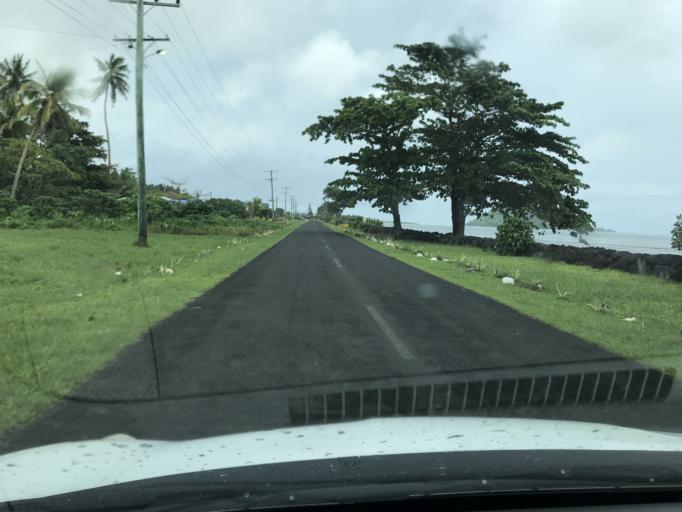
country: WS
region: Va`a-o-Fonoti
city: Samamea
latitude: -14.0425
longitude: -171.4367
